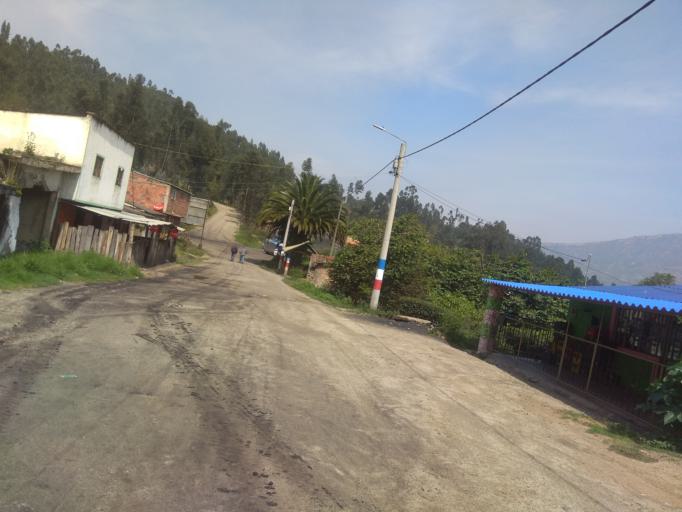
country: CO
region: Boyaca
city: Socha Viejo
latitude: 5.9821
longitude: -72.7121
